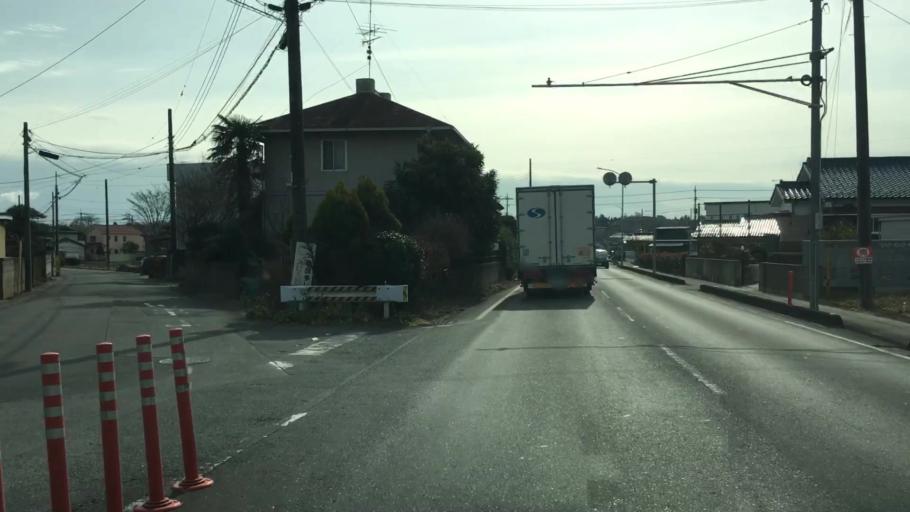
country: JP
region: Saitama
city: Kumagaya
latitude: 36.1327
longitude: 139.3237
